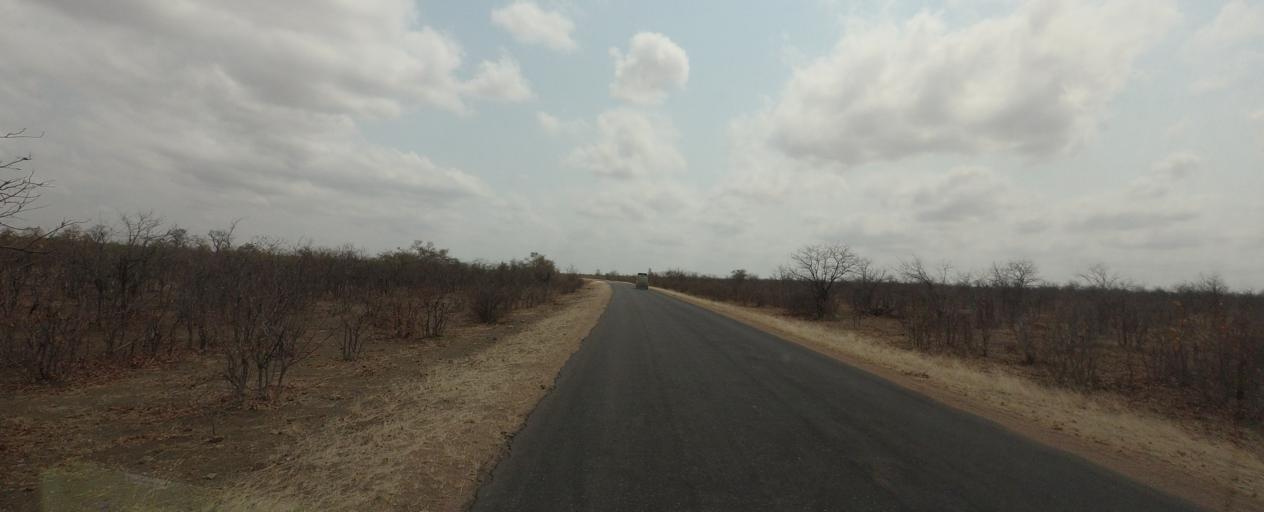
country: ZA
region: Limpopo
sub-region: Mopani District Municipality
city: Phalaborwa
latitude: -23.5970
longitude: 31.4550
